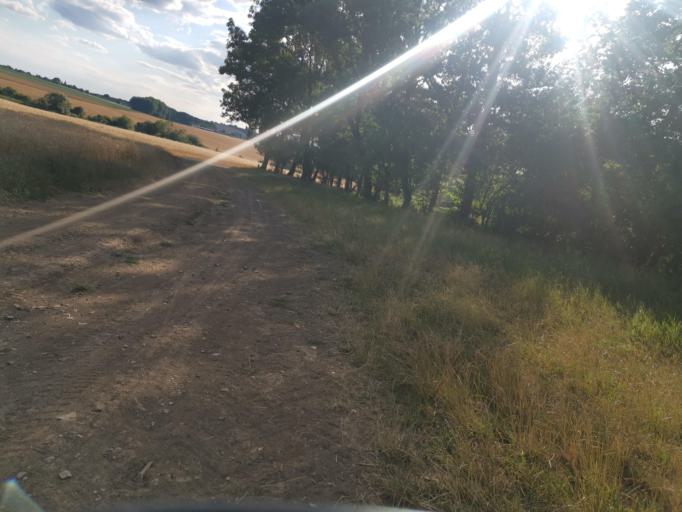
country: SK
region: Trnavsky
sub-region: Okres Skalica
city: Skalica
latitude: 48.8216
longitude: 17.2644
